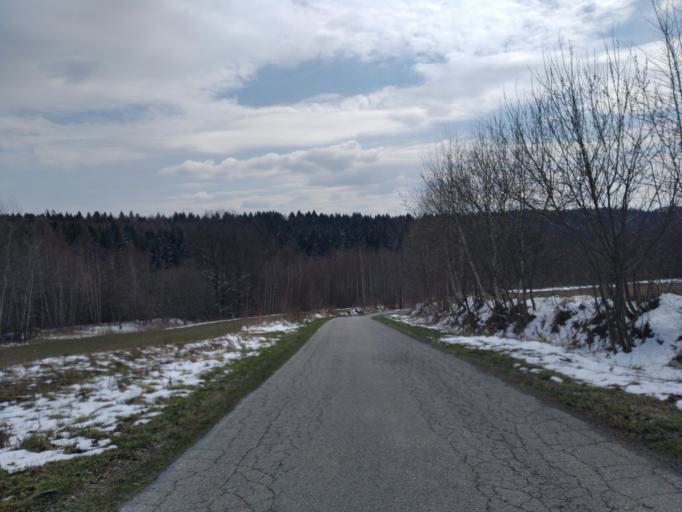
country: PL
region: Subcarpathian Voivodeship
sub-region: Powiat ropczycko-sedziszowski
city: Ropczyce
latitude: 50.0055
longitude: 21.5947
